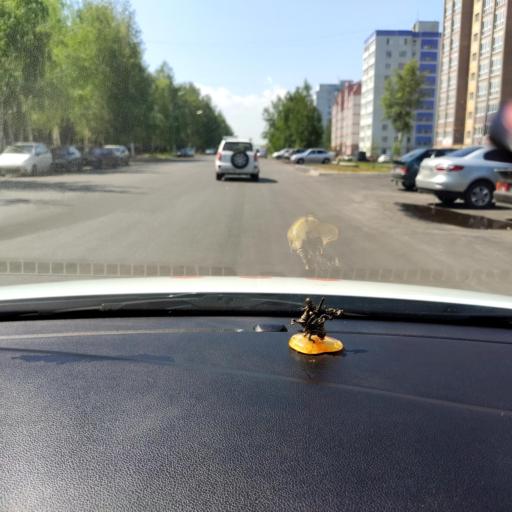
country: RU
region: Tatarstan
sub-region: Zelenodol'skiy Rayon
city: Zelenodolsk
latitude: 55.8557
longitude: 48.5577
